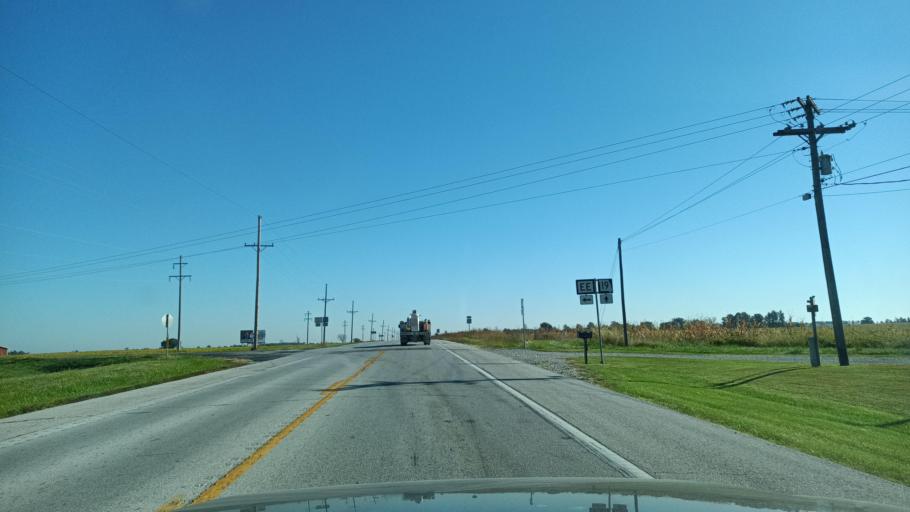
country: US
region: Missouri
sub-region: Audrain County
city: Vandalia
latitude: 39.4642
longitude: -91.6050
